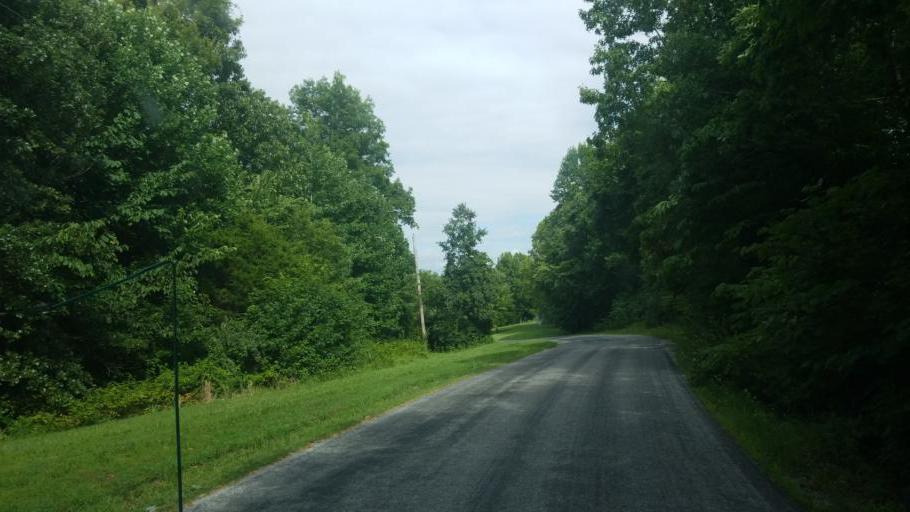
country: US
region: Illinois
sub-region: Union County
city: Cobden
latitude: 37.6121
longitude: -89.3449
